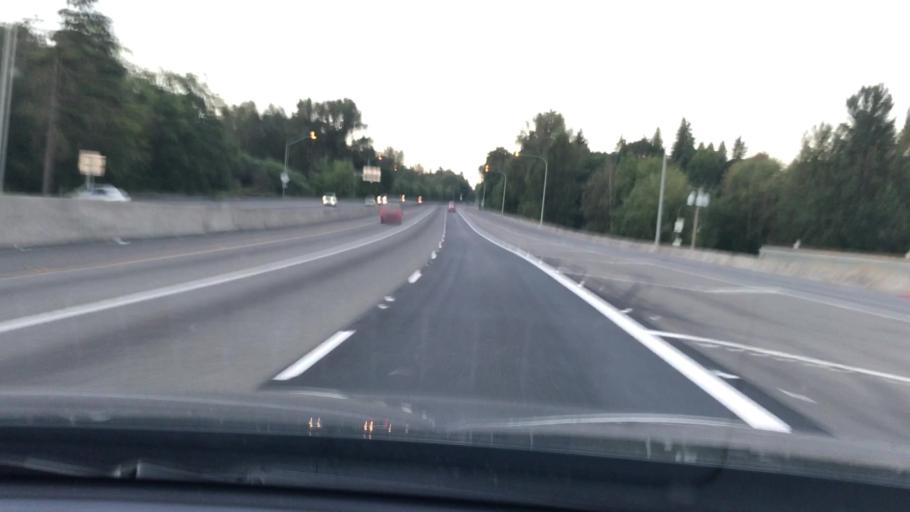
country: US
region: Washington
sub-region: King County
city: Newcastle
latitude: 47.5307
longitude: -122.1980
